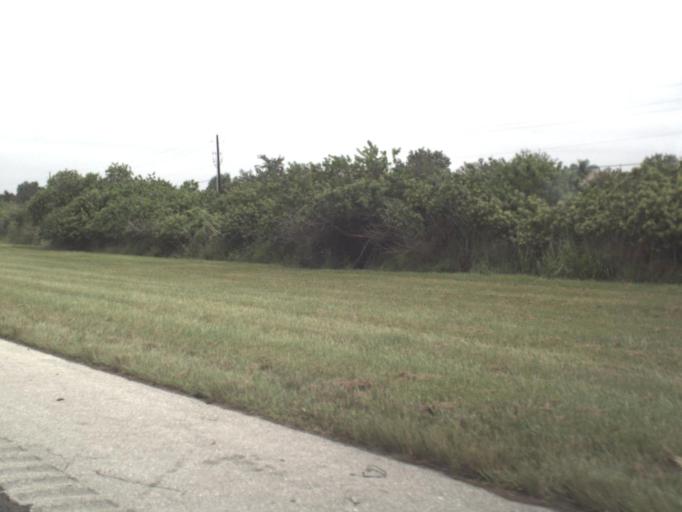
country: US
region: Florida
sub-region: Manatee County
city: Ellenton
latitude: 27.5767
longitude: -82.5143
